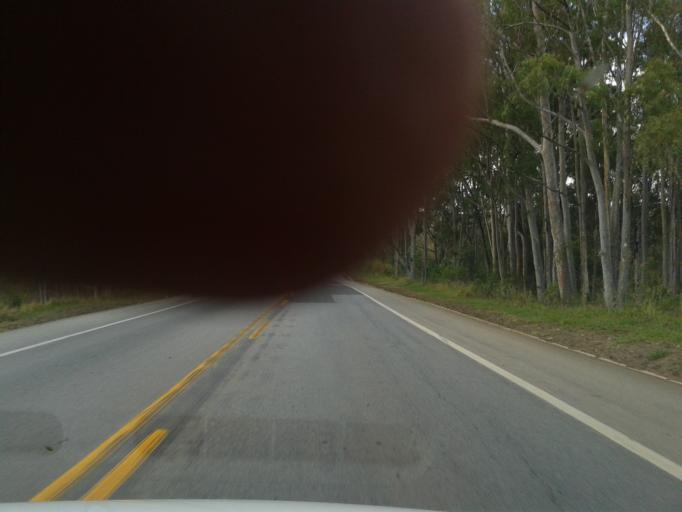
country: BR
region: Minas Gerais
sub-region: Campos Altos
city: Campos Altos
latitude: -19.7140
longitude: -45.9274
